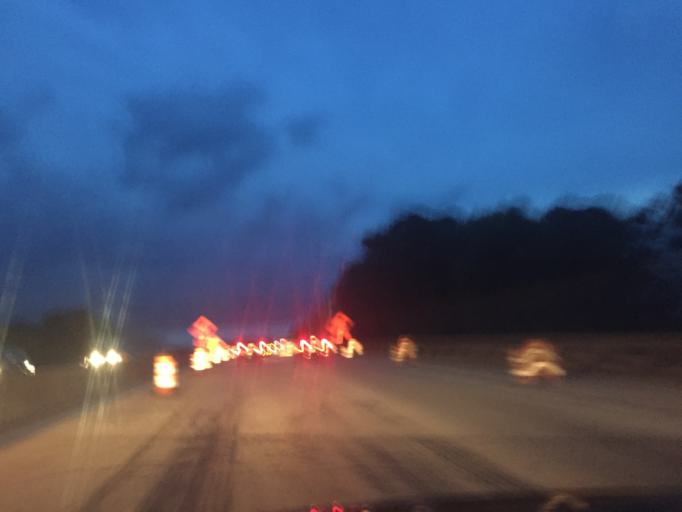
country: US
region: Georgia
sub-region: Chatham County
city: Georgetown
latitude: 31.9888
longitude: -81.2232
